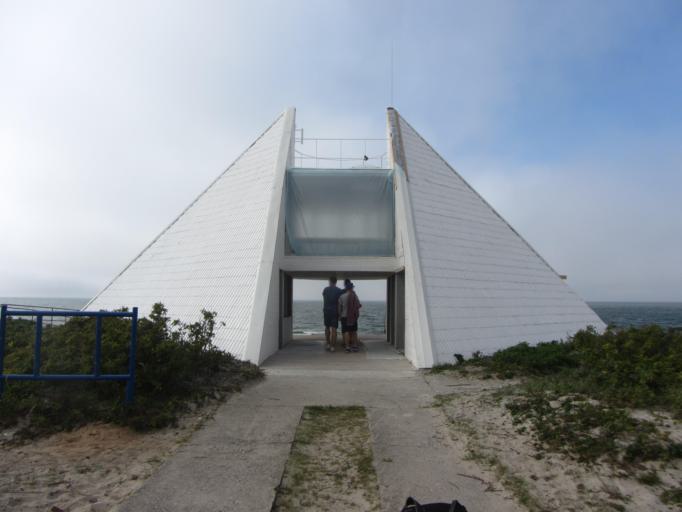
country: LT
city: Neringa
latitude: 55.3775
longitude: 21.0317
